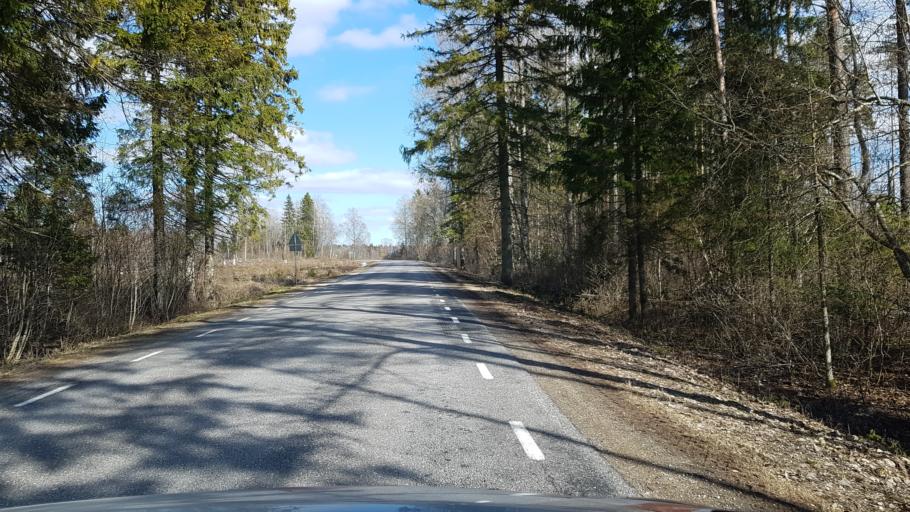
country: EE
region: Laeaene-Virumaa
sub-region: Tapa vald
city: Tapa
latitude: 59.1802
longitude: 26.0052
